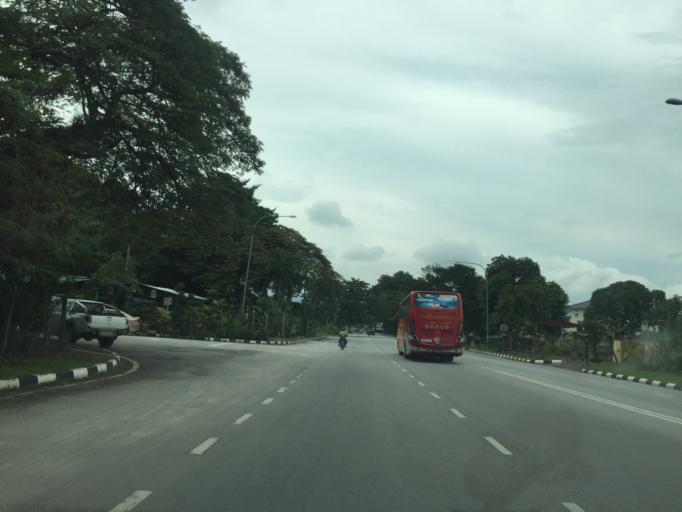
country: MY
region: Perak
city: Ipoh
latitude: 4.5682
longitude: 101.1180
